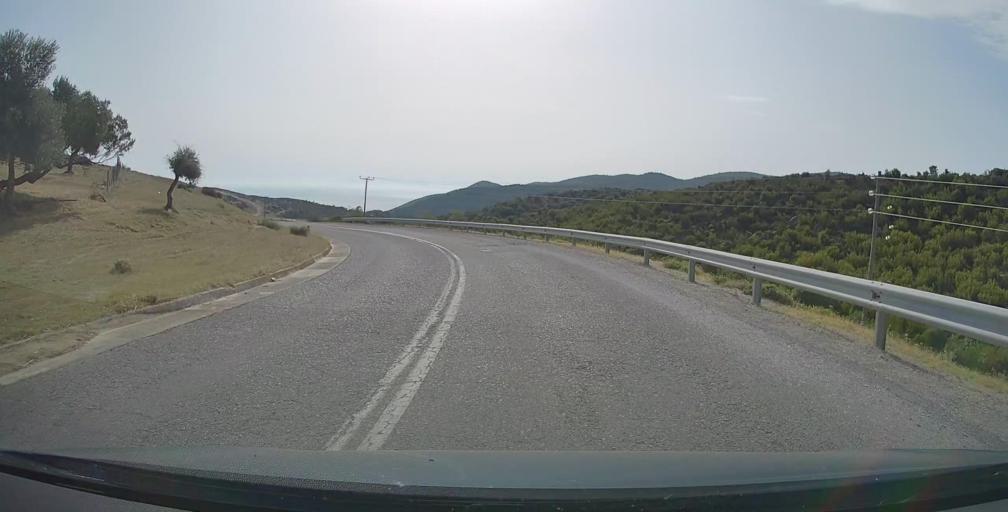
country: GR
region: Central Macedonia
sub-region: Nomos Chalkidikis
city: Sykia
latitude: 39.9912
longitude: 23.9651
